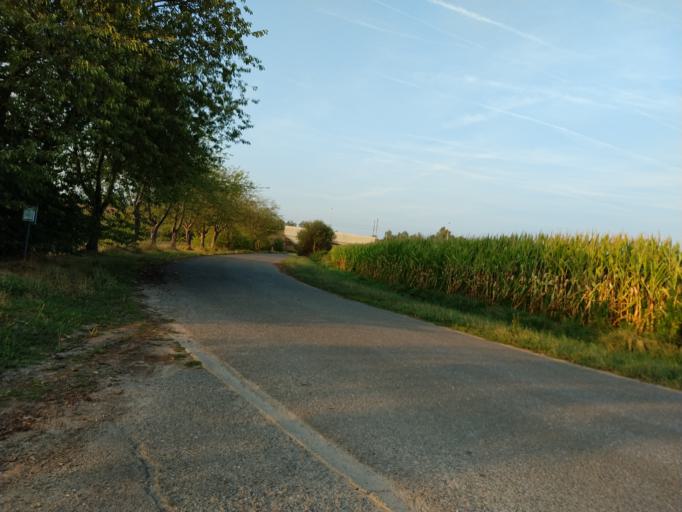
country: BE
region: Flanders
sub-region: Provincie Vlaams-Brabant
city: Hoegaarden
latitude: 50.7829
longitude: 4.9135
